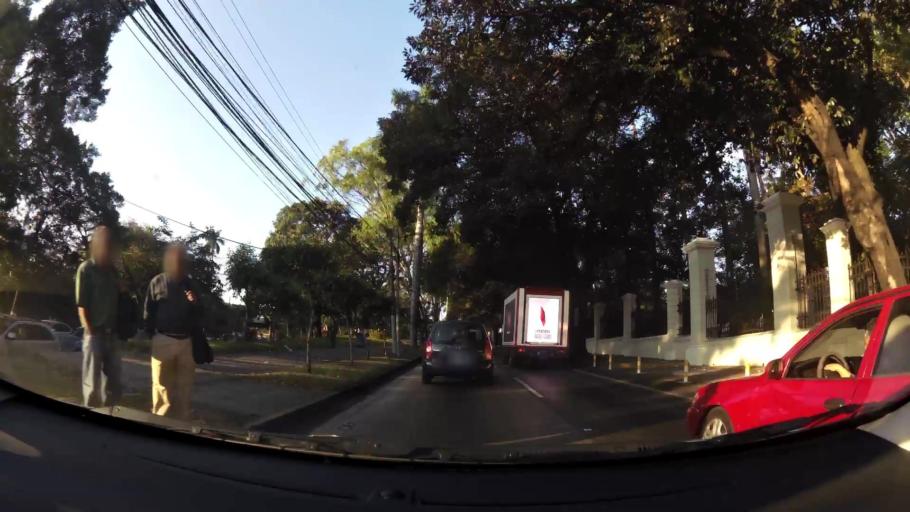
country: SV
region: La Libertad
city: Antiguo Cuscatlan
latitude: 13.6849
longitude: -89.2390
